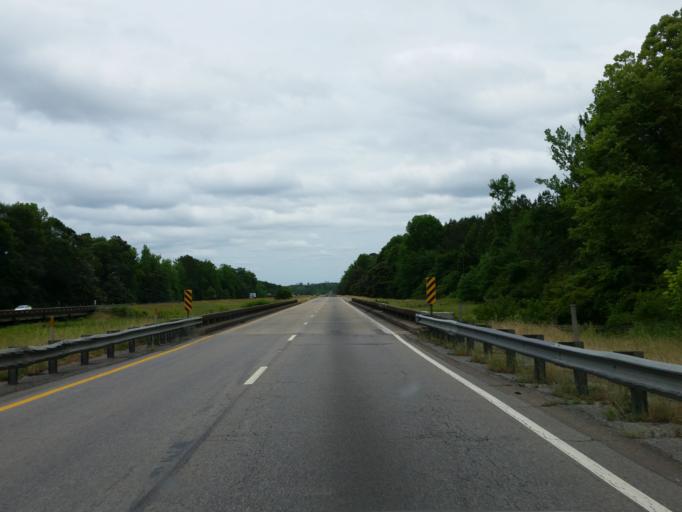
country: US
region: Mississippi
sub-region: Lauderdale County
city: Marion
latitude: 32.4131
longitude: -88.4946
